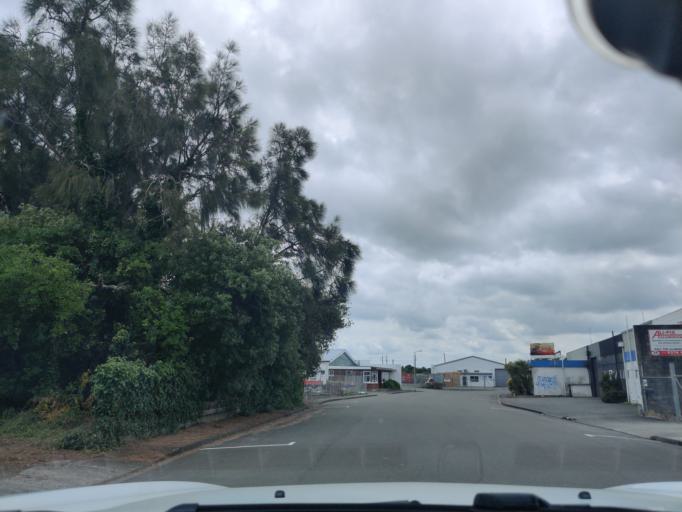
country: NZ
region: Manawatu-Wanganui
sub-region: Palmerston North City
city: Palmerston North
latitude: -40.3489
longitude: 175.5885
